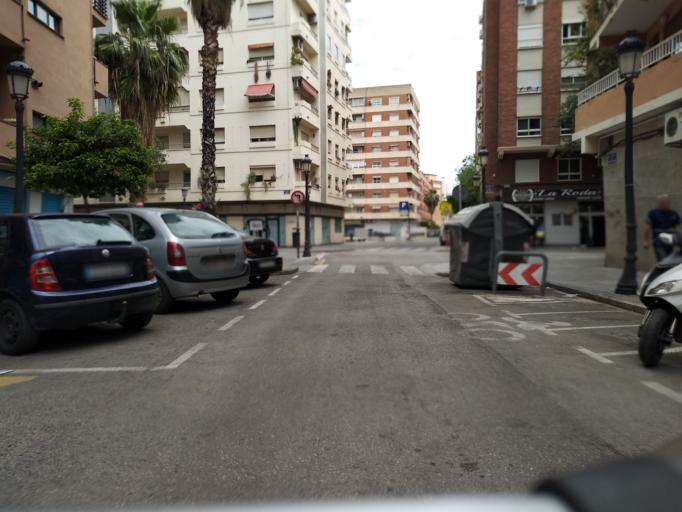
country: ES
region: Valencia
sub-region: Provincia de Valencia
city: Tavernes Blanques
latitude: 39.4889
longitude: -0.3723
